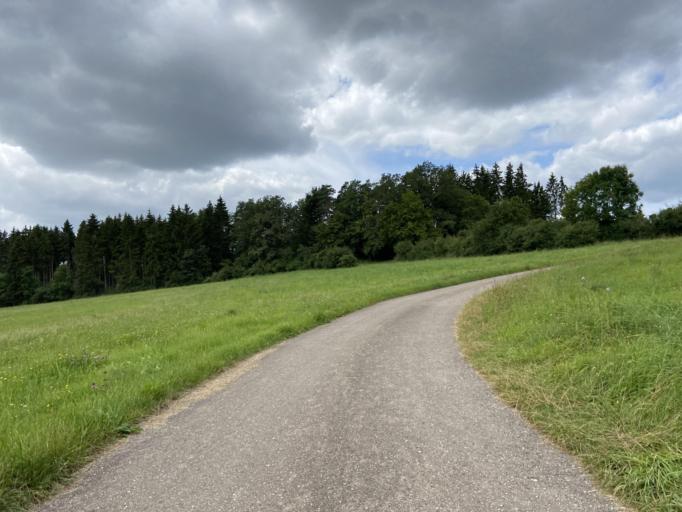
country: DE
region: Baden-Wuerttemberg
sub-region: Tuebingen Region
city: Bingen
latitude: 48.0971
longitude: 9.2907
